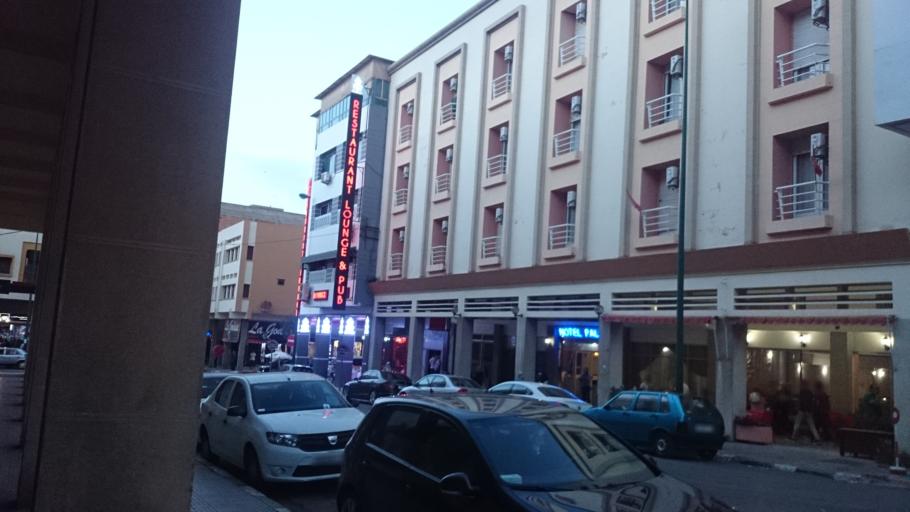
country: MA
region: Meknes-Tafilalet
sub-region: Meknes
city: Meknes
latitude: 33.8983
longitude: -5.5495
